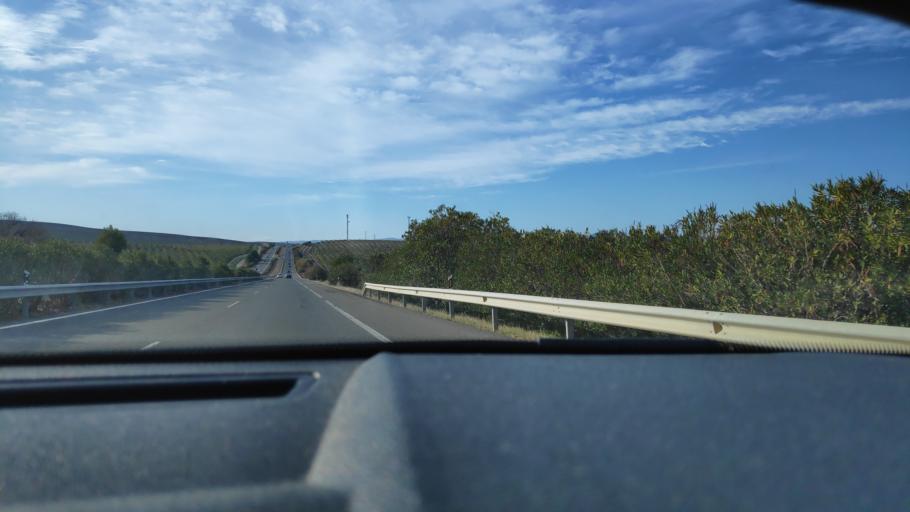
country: ES
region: Andalusia
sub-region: Province of Cordoba
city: Villafranca de Cordoba
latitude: 37.9046
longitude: -4.6182
